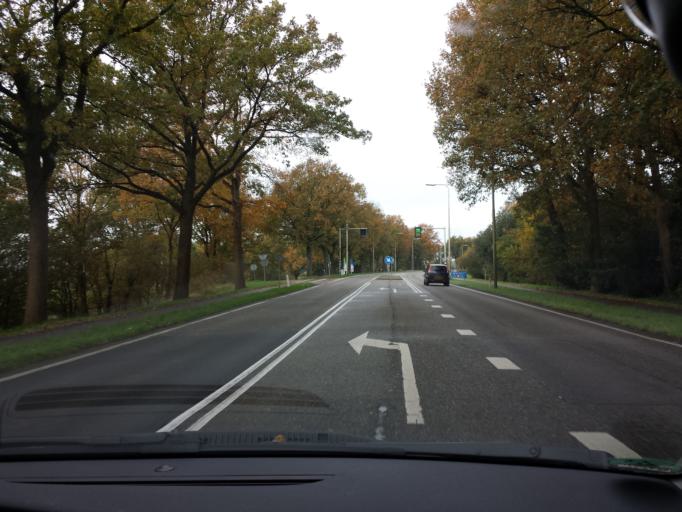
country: NL
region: North Brabant
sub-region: Gemeente Boxmeer
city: Boxmeer
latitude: 51.6341
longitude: 6.0072
